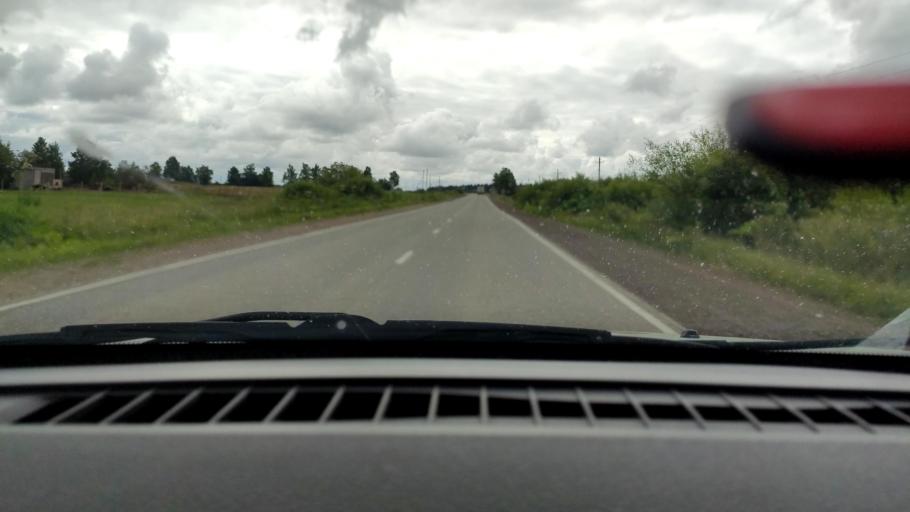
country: RU
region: Perm
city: Ust'-Kachka
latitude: 58.0725
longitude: 55.6236
